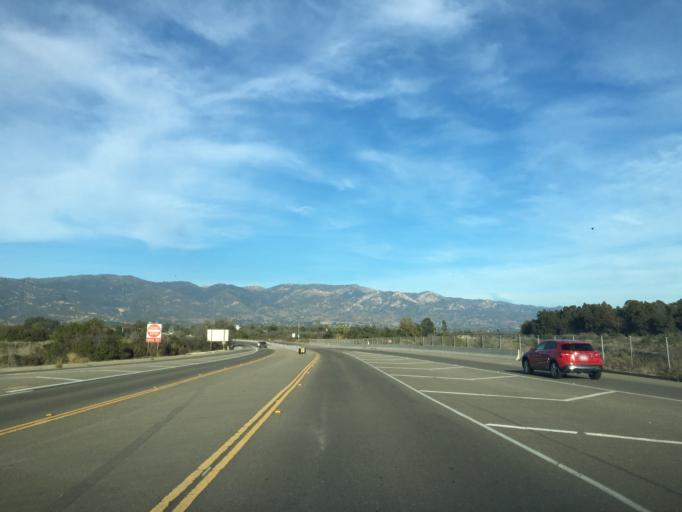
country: US
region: California
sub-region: Santa Barbara County
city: Goleta
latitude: 34.4198
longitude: -119.8311
